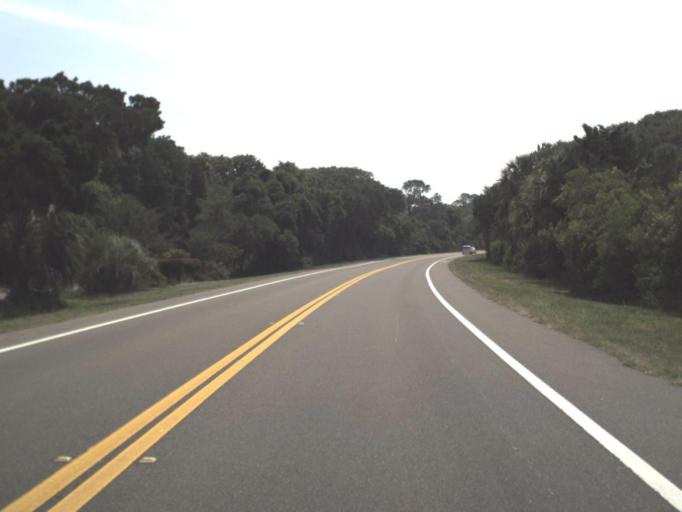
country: US
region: Florida
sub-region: Nassau County
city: Fernandina Beach
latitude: 30.5312
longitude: -81.4398
